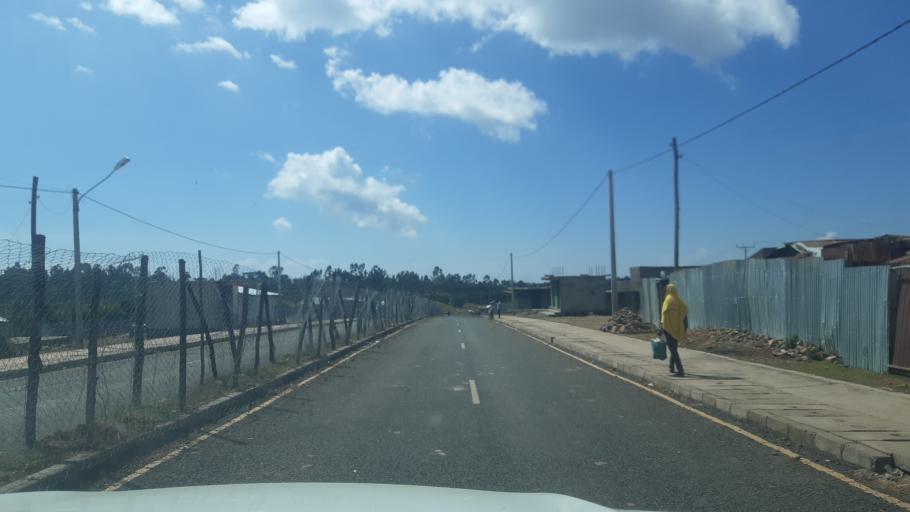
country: ET
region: Amhara
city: Dabat
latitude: 13.3919
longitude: 37.3997
